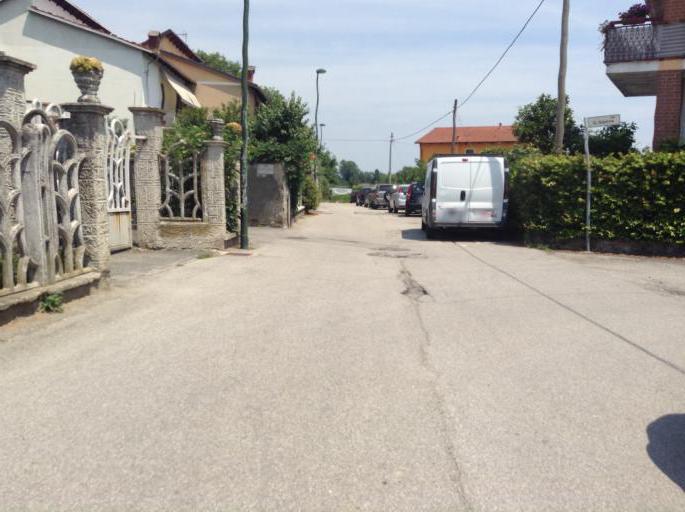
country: IT
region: Piedmont
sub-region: Provincia di Torino
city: Carignano
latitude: 44.9067
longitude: 7.6814
